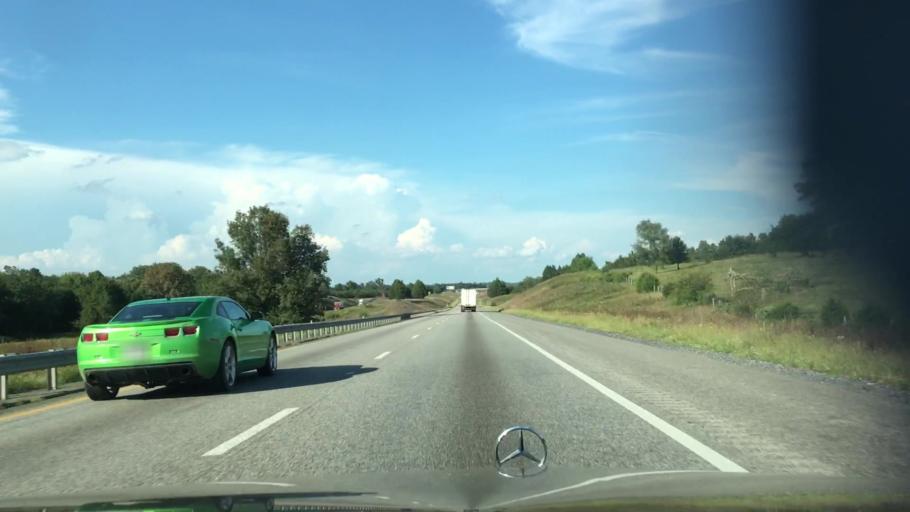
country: US
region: Virginia
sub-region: Rockingham County
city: Broadway
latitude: 38.5219
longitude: -78.7745
